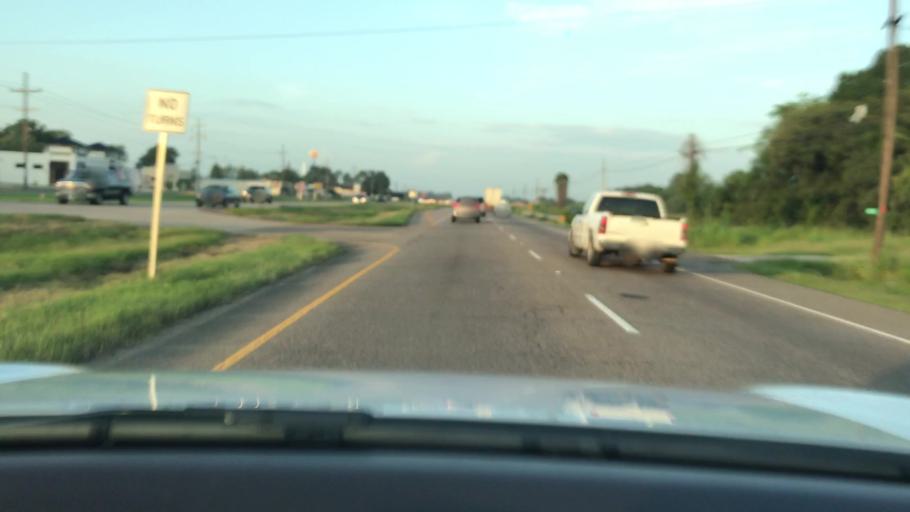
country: US
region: Louisiana
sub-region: West Baton Rouge Parish
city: Brusly
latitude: 30.4098
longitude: -91.2281
